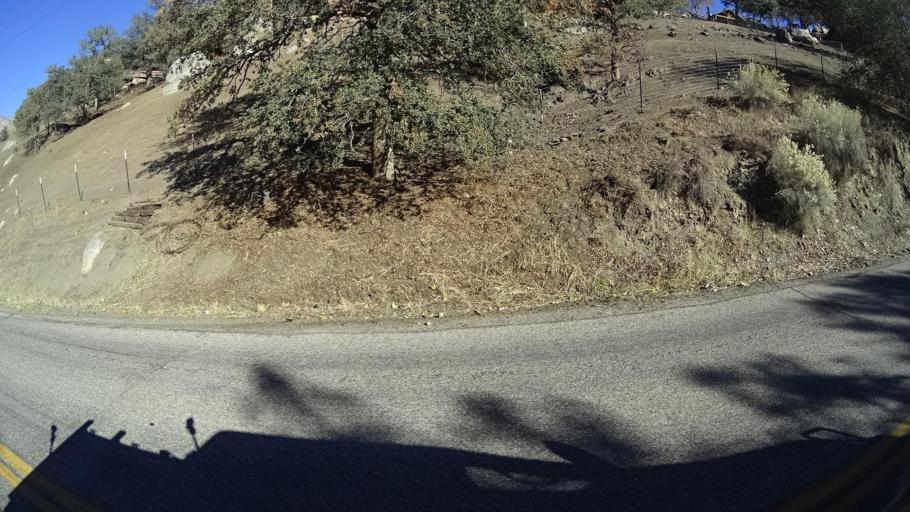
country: US
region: California
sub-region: Kern County
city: Kernville
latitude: 35.7621
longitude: -118.4211
